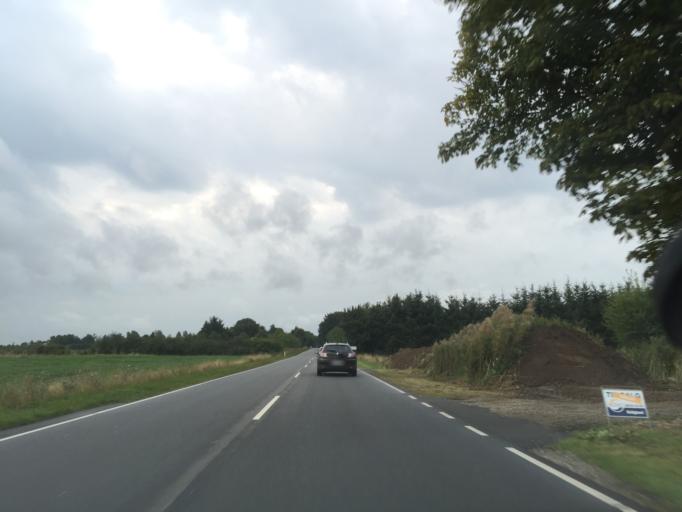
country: DK
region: Central Jutland
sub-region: Skanderborg Kommune
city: Galten
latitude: 56.1014
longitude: 9.8950
